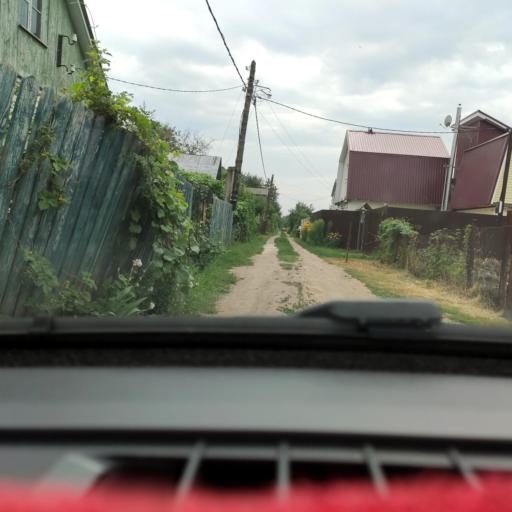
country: RU
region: Voronezj
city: Maslovka
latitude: 51.5887
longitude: 39.1721
